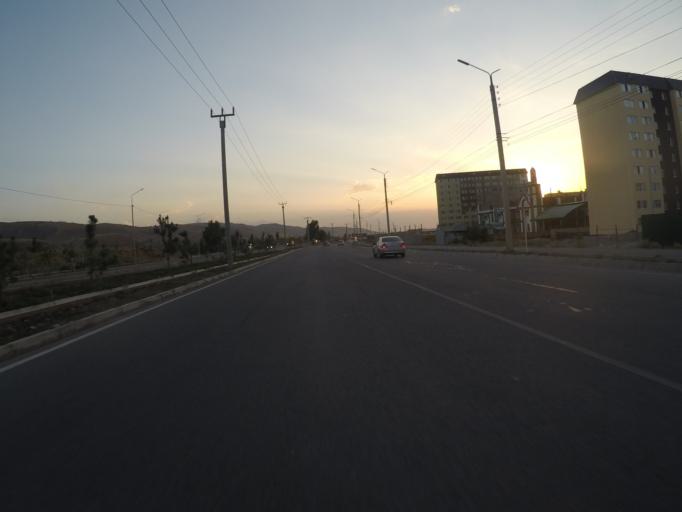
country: KG
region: Chuy
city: Bishkek
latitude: 42.8111
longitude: 74.6385
